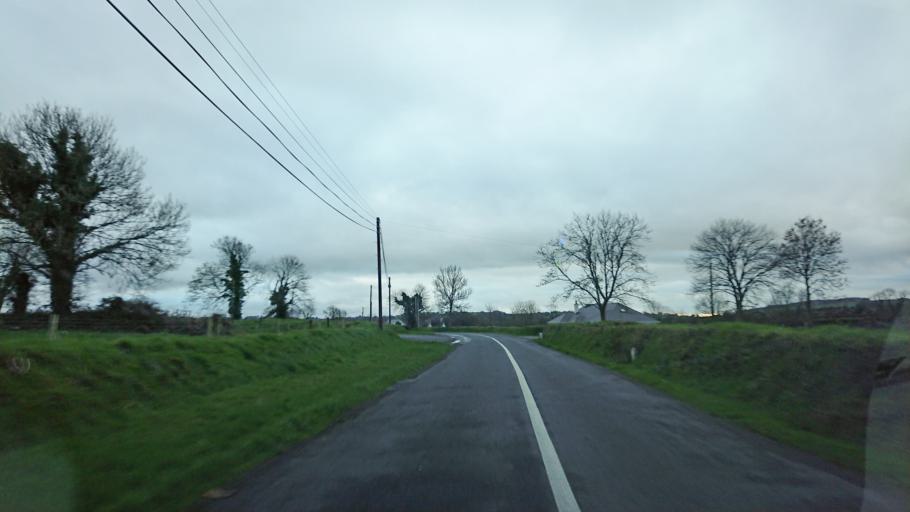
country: IE
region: Munster
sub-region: Waterford
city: Portlaw
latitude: 52.1842
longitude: -7.4086
